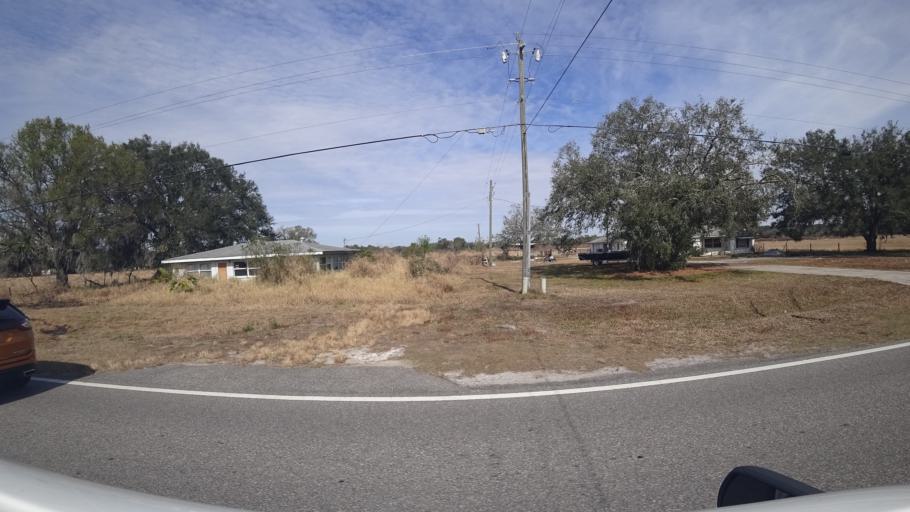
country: US
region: Florida
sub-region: Manatee County
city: Ellenton
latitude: 27.5758
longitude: -82.4031
